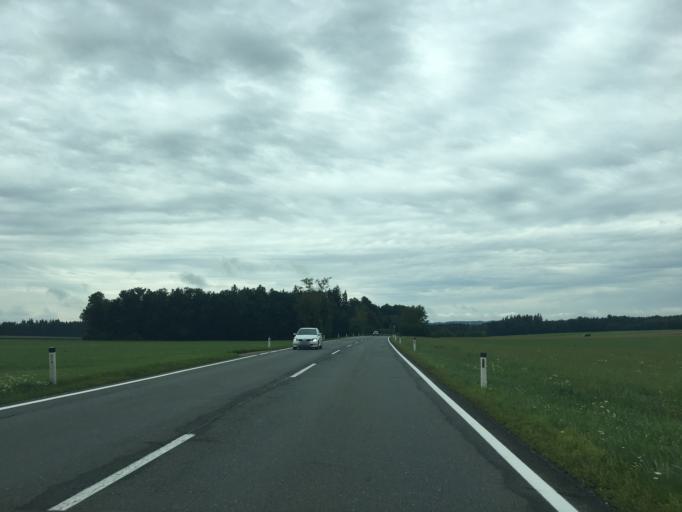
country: AT
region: Salzburg
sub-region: Politischer Bezirk Salzburg-Umgebung
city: Lamprechtshausen
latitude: 48.0139
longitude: 12.9652
